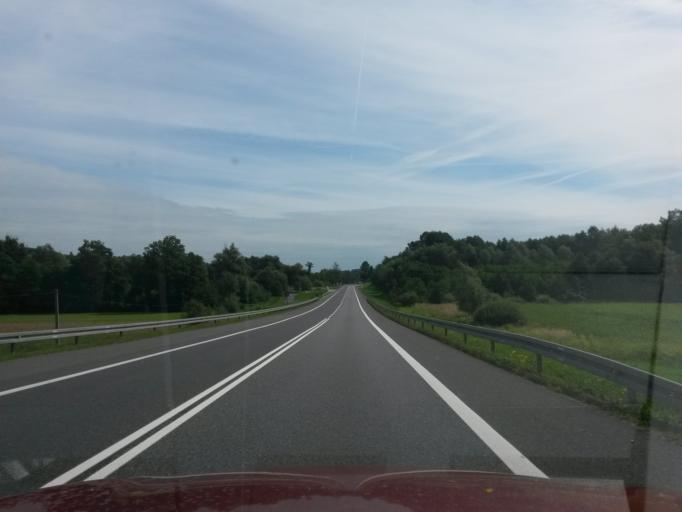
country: PL
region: Lesser Poland Voivodeship
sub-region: Powiat bochenski
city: Stanislawice
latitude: 49.9630
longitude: 20.3512
